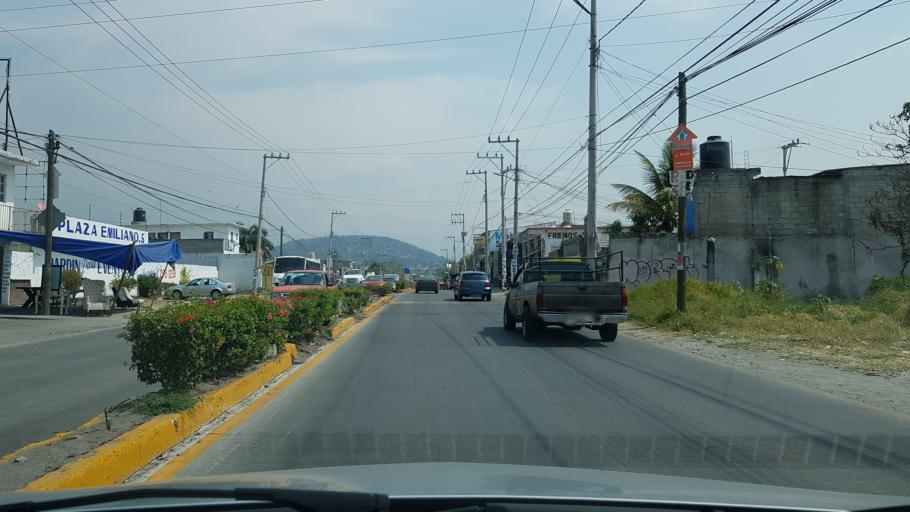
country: MX
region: Morelos
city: Emiliano Zapata
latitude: 18.8216
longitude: -99.1899
